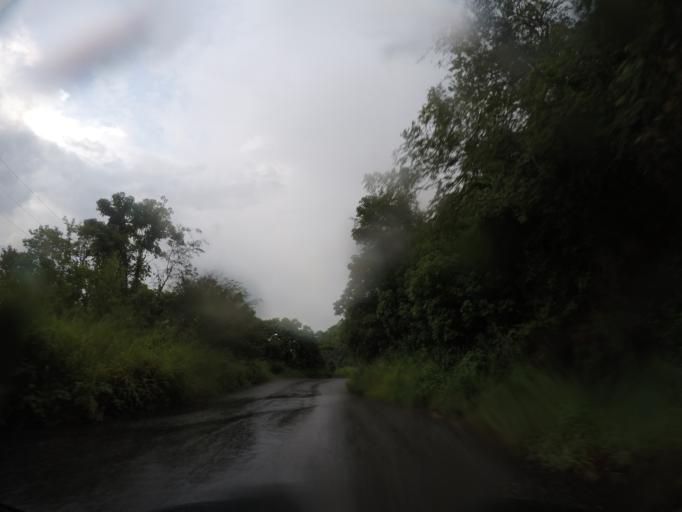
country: MX
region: Oaxaca
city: San Gabriel Mixtepec
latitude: 16.0622
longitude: -97.0757
